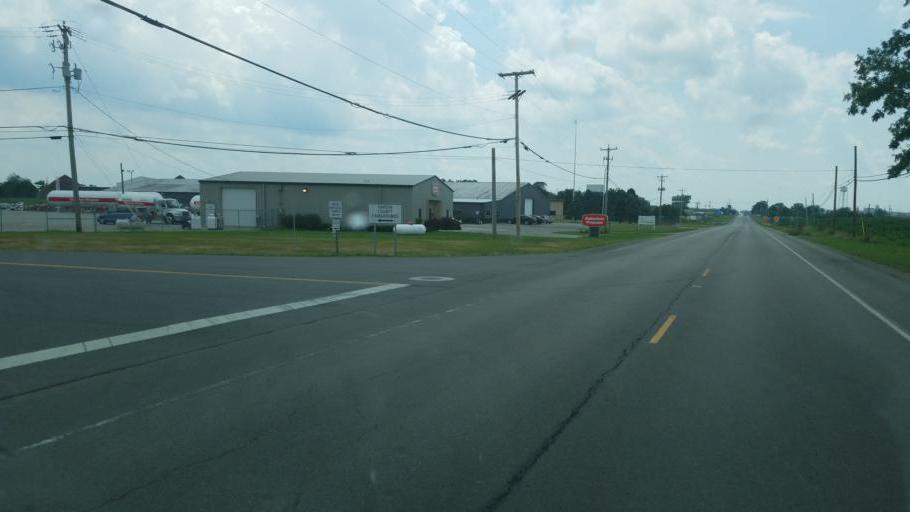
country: US
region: Ohio
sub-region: Hardin County
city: Kenton
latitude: 40.6327
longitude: -83.6150
